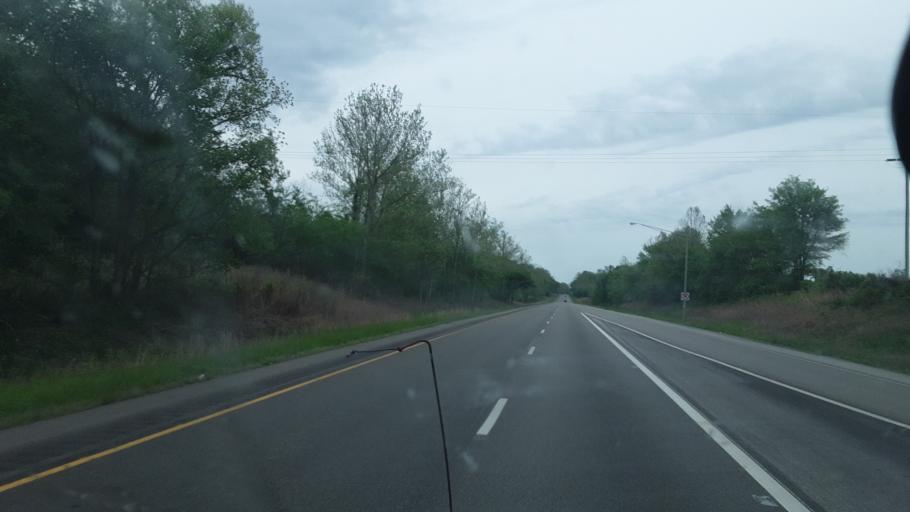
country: US
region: Indiana
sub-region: Posey County
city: Poseyville
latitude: 38.1953
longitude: -87.8561
